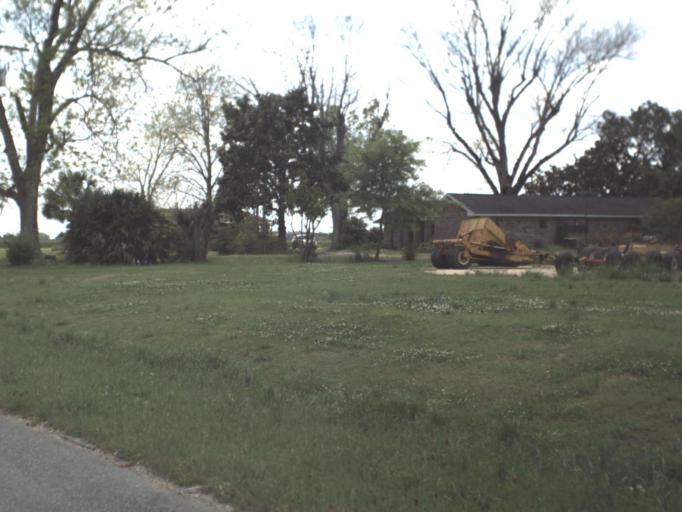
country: US
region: Alabama
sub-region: Escambia County
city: Atmore
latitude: 30.9794
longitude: -87.4909
